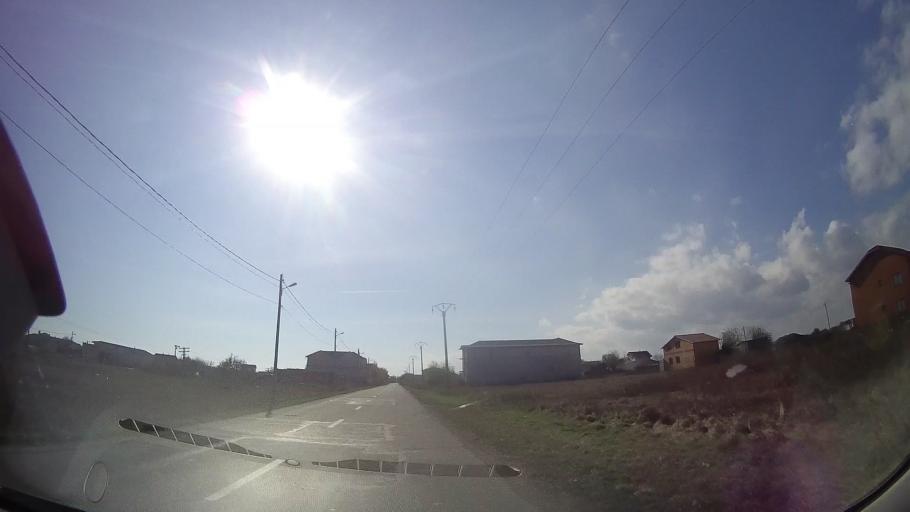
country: RO
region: Constanta
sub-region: Comuna Costinesti
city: Costinesti
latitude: 43.9574
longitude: 28.6342
